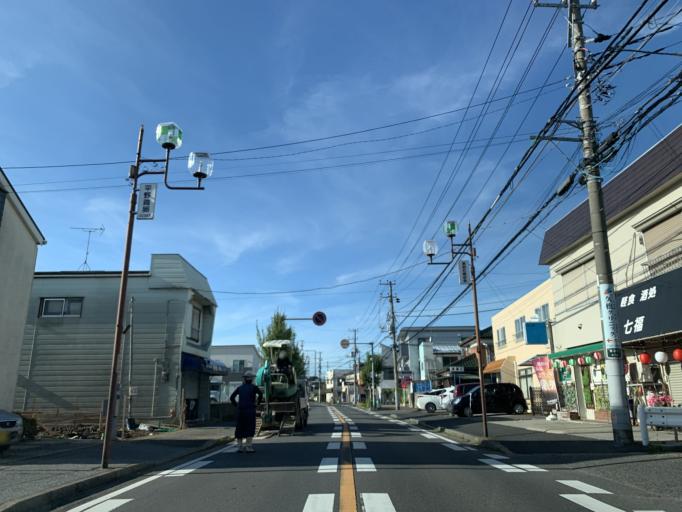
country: JP
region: Chiba
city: Nagareyama
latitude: 35.8851
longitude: 139.9216
